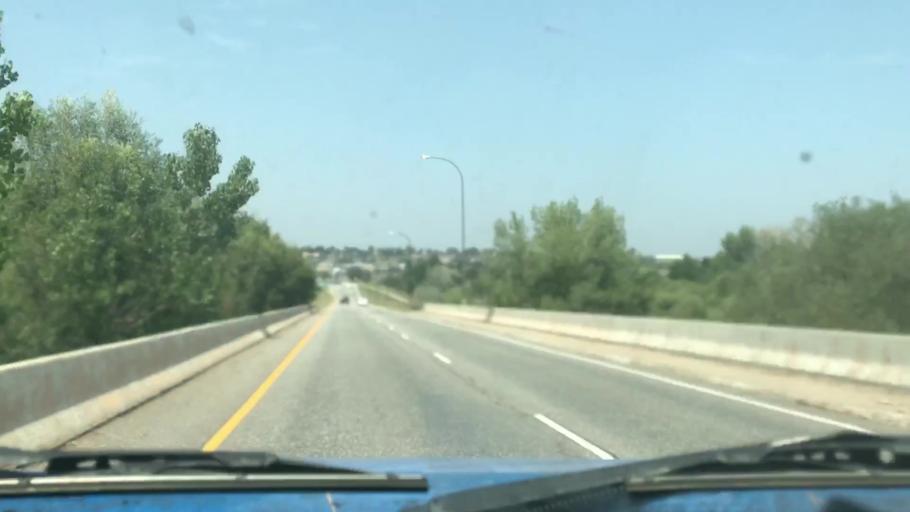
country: US
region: Colorado
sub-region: Jefferson County
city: Lakewood
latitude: 39.6620
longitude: -105.1125
